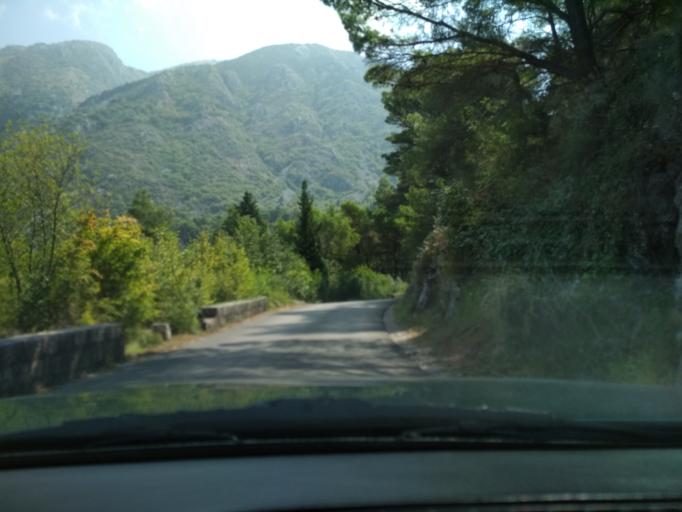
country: ME
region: Kotor
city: Kotor
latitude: 42.3992
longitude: 18.7641
